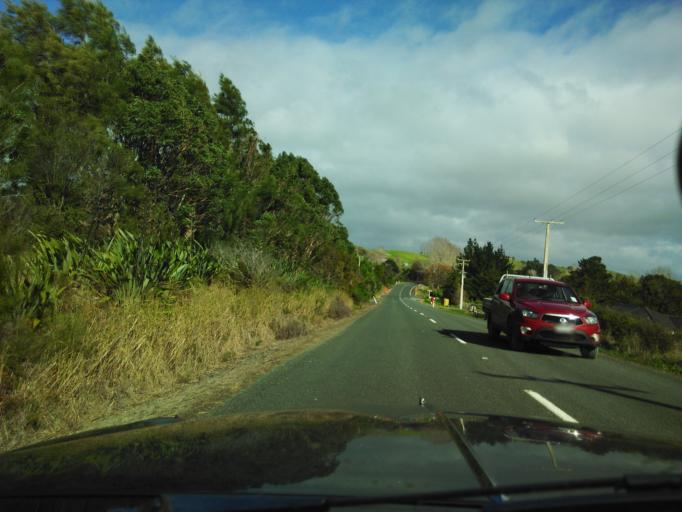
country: NZ
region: Auckland
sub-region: Auckland
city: Wellsford
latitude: -36.1765
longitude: 174.4152
